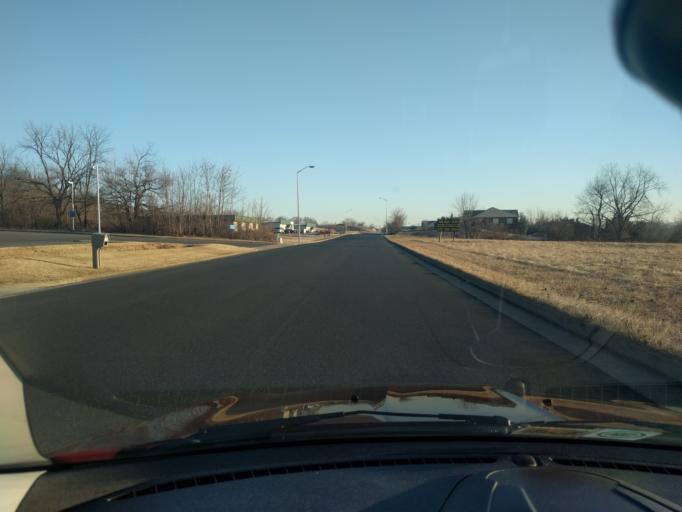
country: US
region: Virginia
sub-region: Rockingham County
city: Dayton
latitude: 38.4076
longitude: -78.9097
